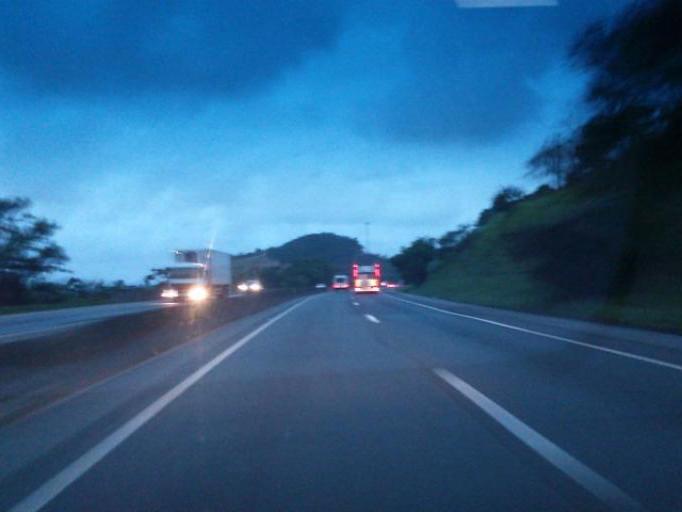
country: BR
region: Santa Catarina
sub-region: Barra Velha
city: Barra Velha
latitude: -26.7006
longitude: -48.6991
